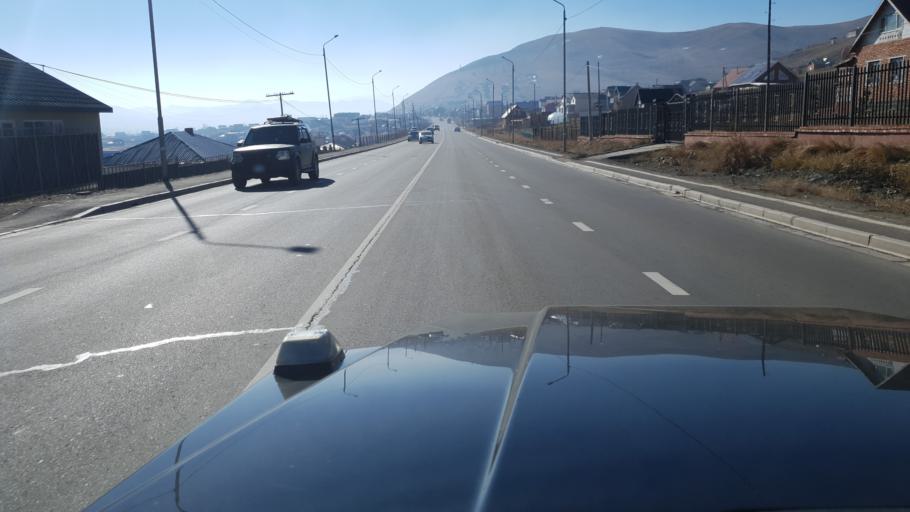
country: MN
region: Ulaanbaatar
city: Ulaanbaatar
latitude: 48.0223
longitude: 106.9145
